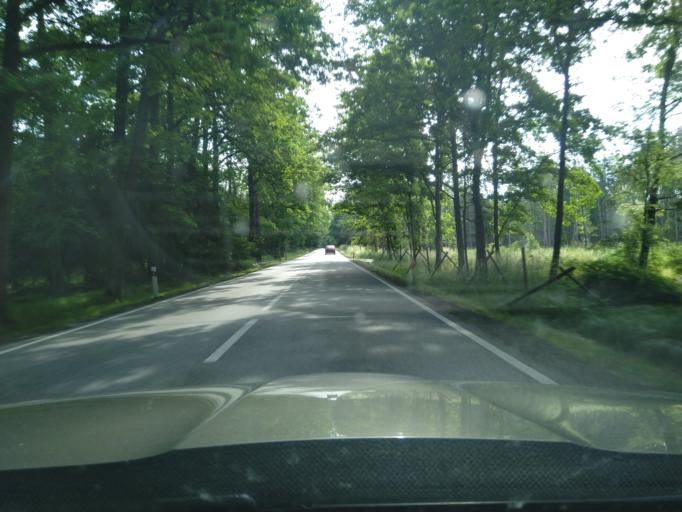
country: CZ
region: Jihocesky
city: Zliv
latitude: 49.0303
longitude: 14.3183
